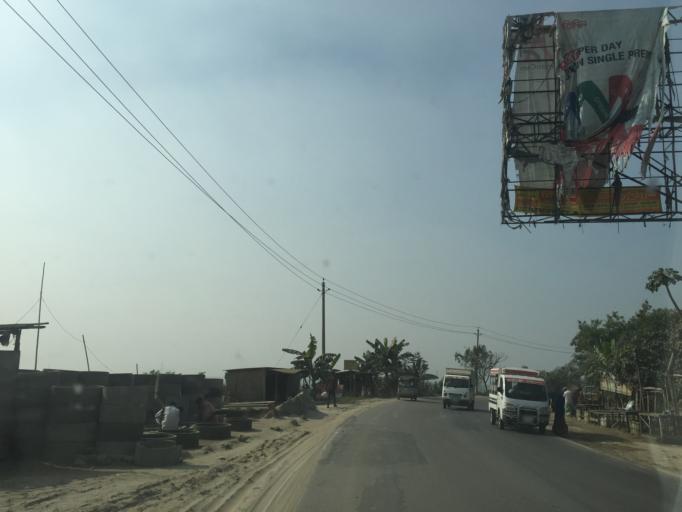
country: BD
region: Dhaka
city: Tungi
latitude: 23.8287
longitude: 90.3439
